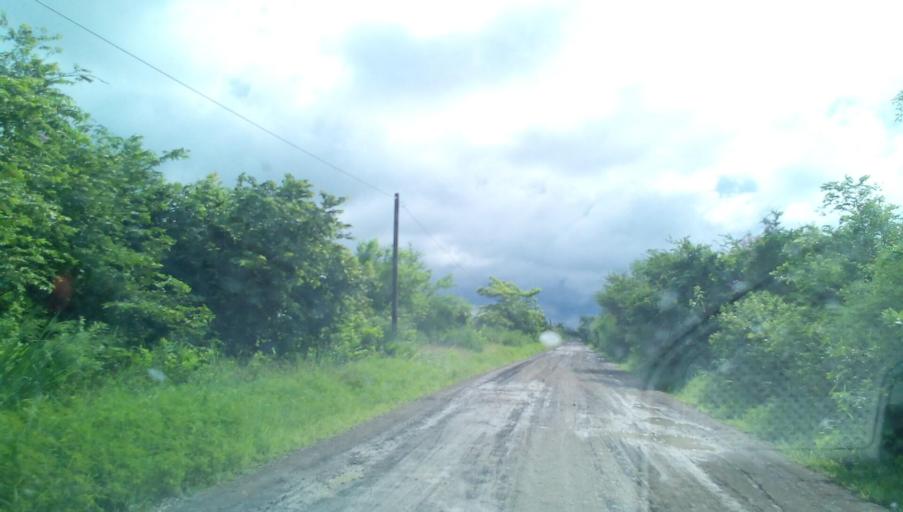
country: MX
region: Veracruz
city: Panuco
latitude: 21.8505
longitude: -98.1598
